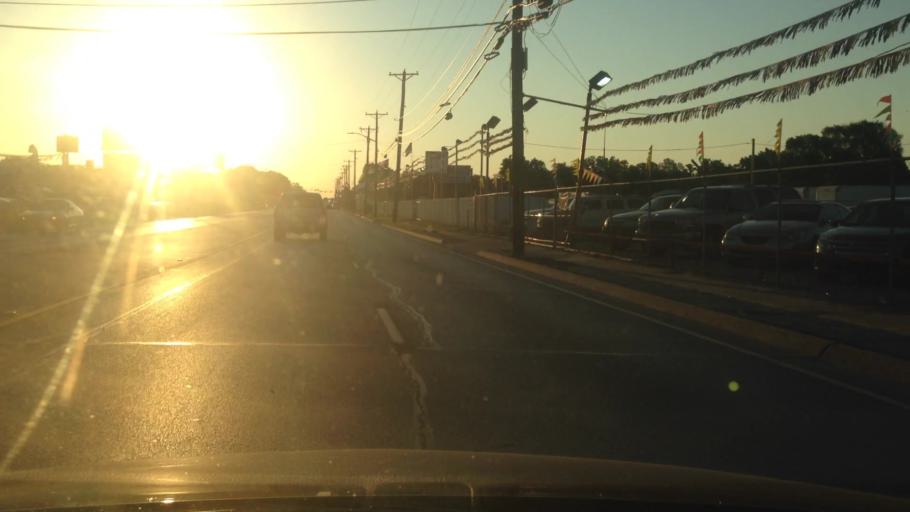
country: US
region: Texas
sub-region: Tarrant County
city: Haltom City
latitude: 32.7951
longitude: -97.2971
